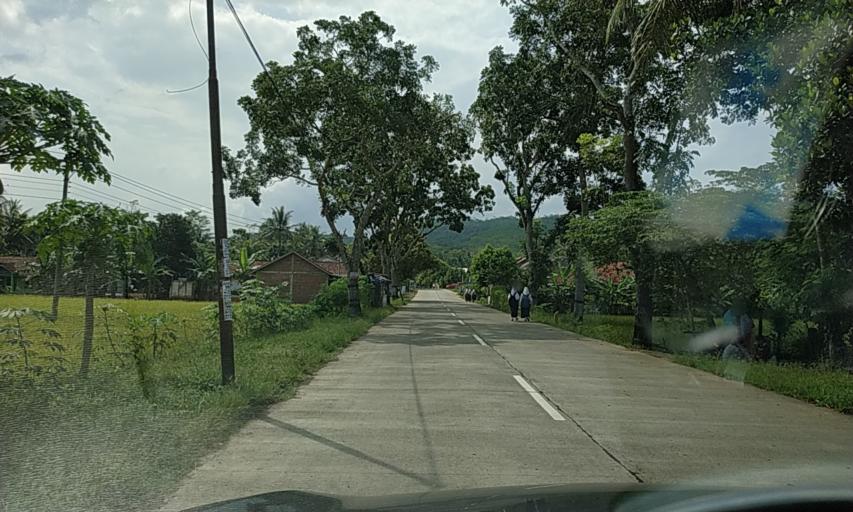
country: ID
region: Central Java
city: Winangun
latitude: -7.3457
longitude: 108.7085
